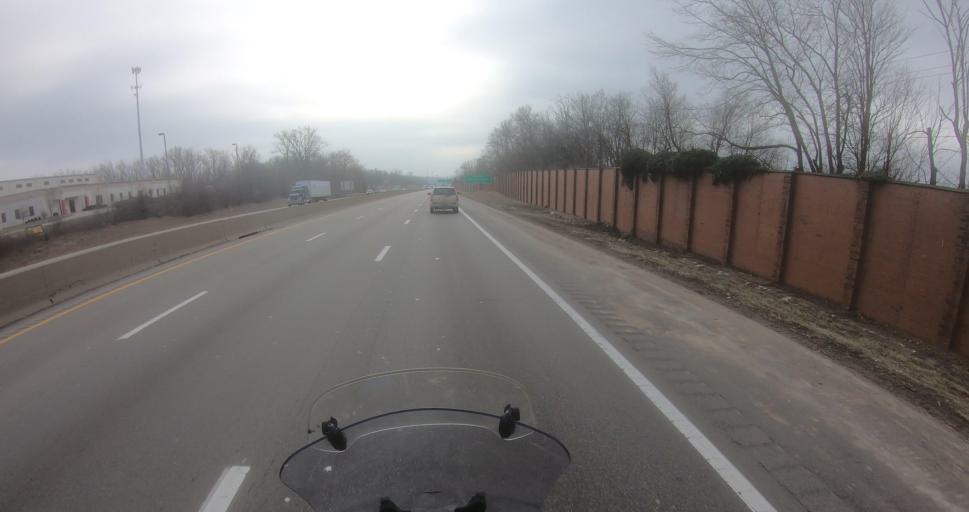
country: US
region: Ohio
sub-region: Montgomery County
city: Vandalia
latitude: 39.8808
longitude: -84.1876
